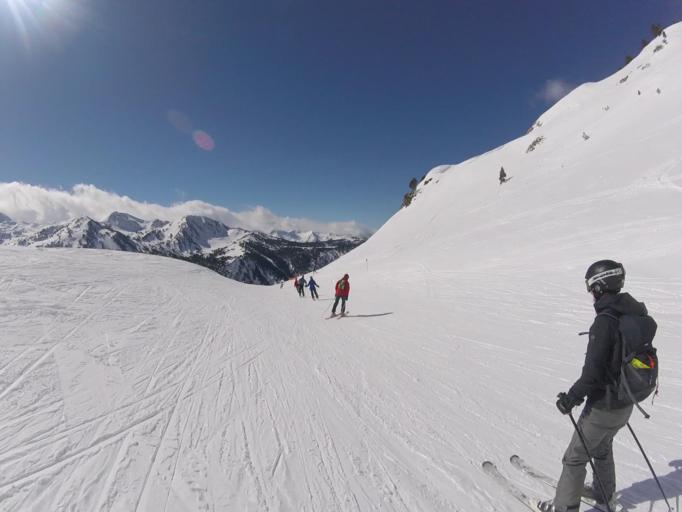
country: ES
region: Catalonia
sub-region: Provincia de Lleida
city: Espot
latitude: 42.6691
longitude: 0.9828
